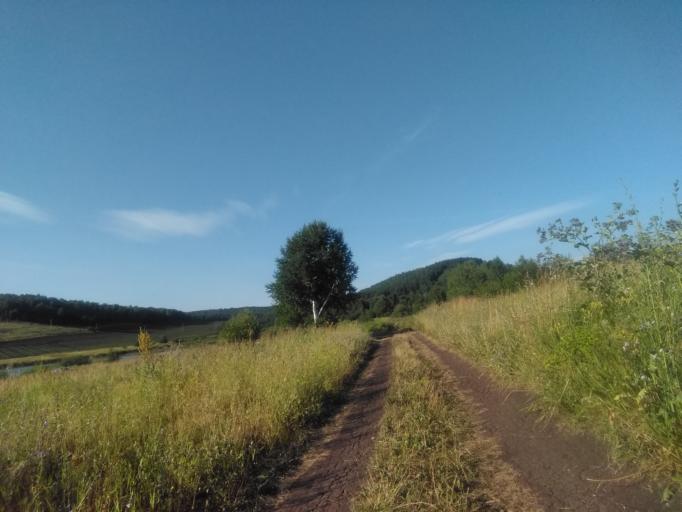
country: RU
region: Tatarstan
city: Russkiy Aktash
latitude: 54.8803
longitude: 52.0742
